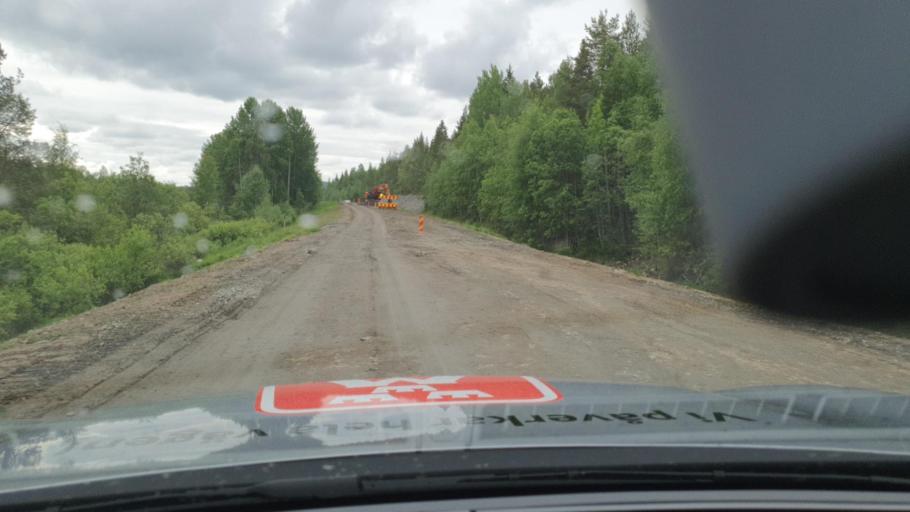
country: SE
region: Norrbotten
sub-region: Overtornea Kommun
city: OEvertornea
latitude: 66.4100
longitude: 23.6034
